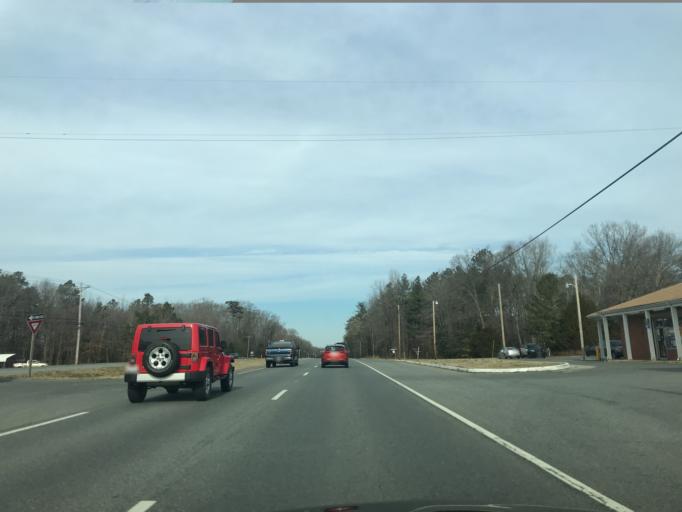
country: US
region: Maryland
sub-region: Charles County
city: La Plata
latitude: 38.4192
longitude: -76.9612
